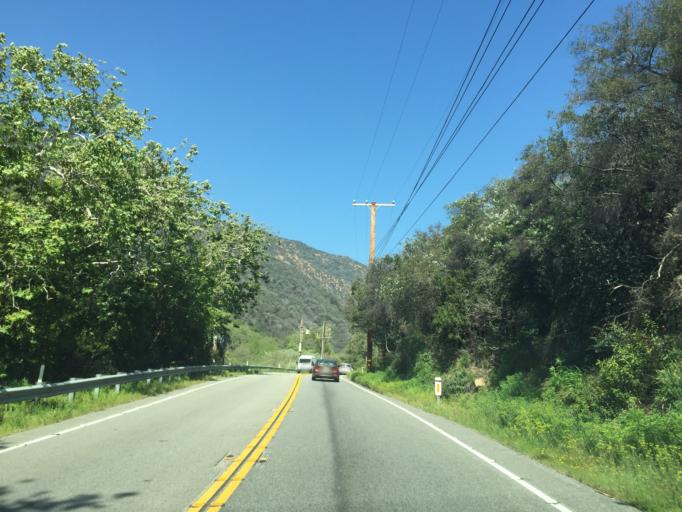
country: US
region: California
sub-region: Los Angeles County
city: Topanga
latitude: 34.0562
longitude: -118.5829
